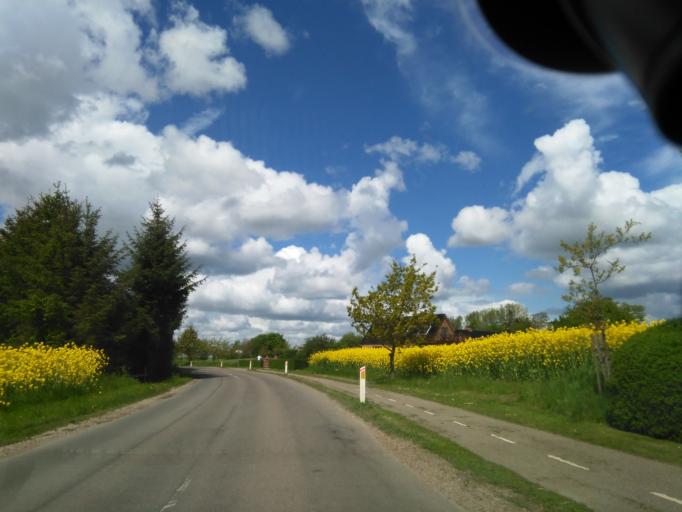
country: DK
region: Central Jutland
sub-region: Skanderborg Kommune
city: Horning
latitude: 56.0694
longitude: 10.0648
